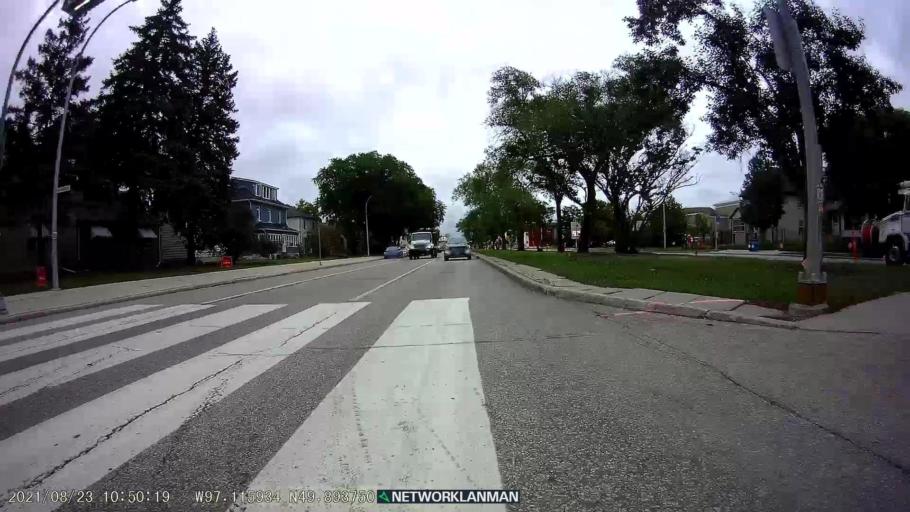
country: CA
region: Manitoba
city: Winnipeg
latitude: 49.8936
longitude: -97.1163
